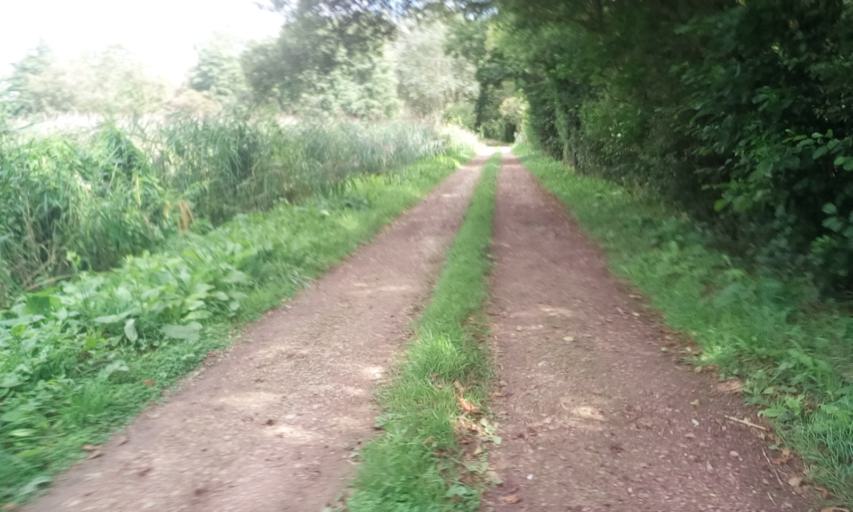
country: FR
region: Lower Normandy
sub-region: Departement du Calvados
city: Bellengreville
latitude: 49.1147
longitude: -0.2234
